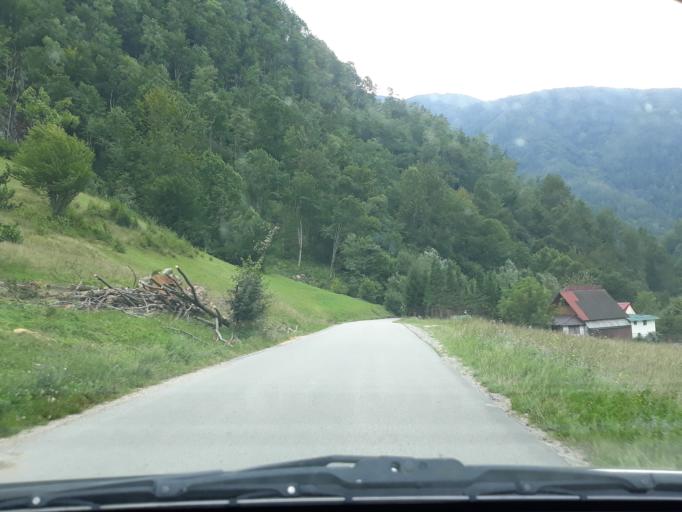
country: RO
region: Bihor
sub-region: Comuna Pietroasa
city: Pietroasa
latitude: 46.5954
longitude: 22.6363
